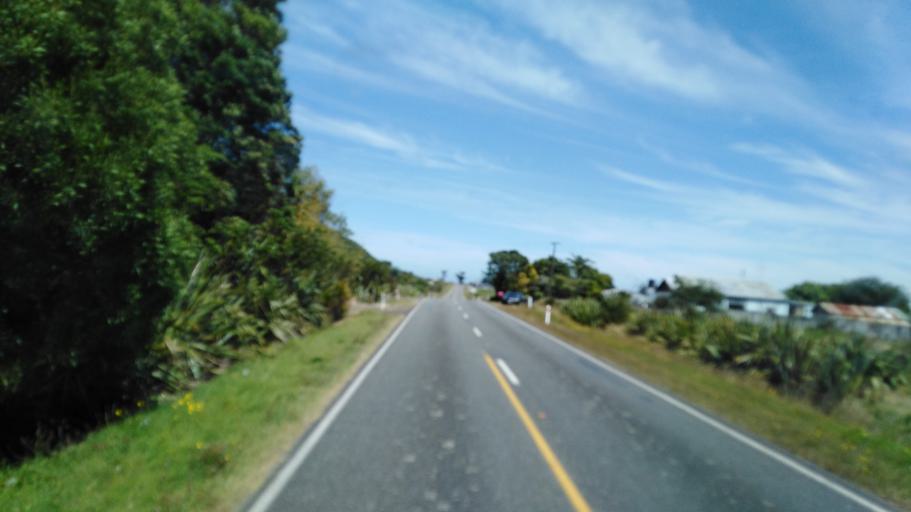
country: NZ
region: West Coast
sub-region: Buller District
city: Westport
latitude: -41.5314
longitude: 171.9404
